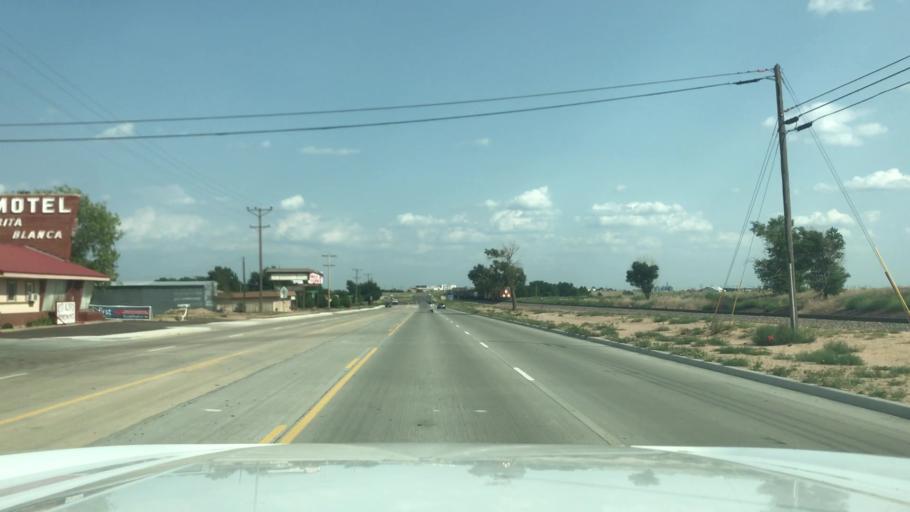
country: US
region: Texas
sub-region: Dallam County
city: Dalhart
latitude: 36.0496
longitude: -102.4987
